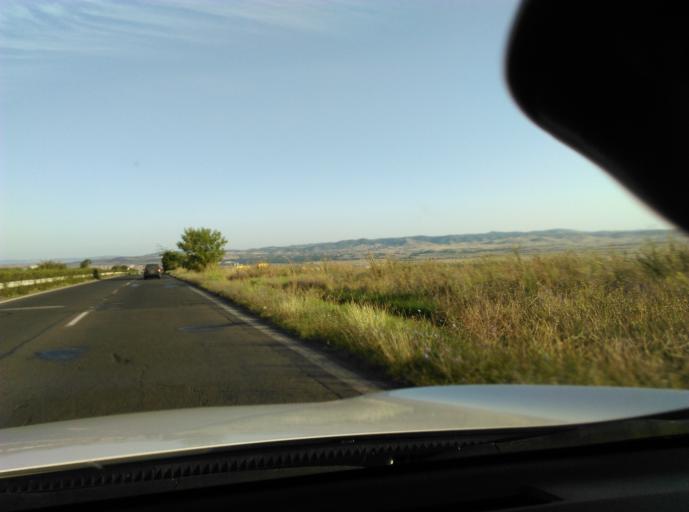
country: BG
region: Burgas
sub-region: Obshtina Burgas
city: Burgas
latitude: 42.5658
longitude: 27.4188
